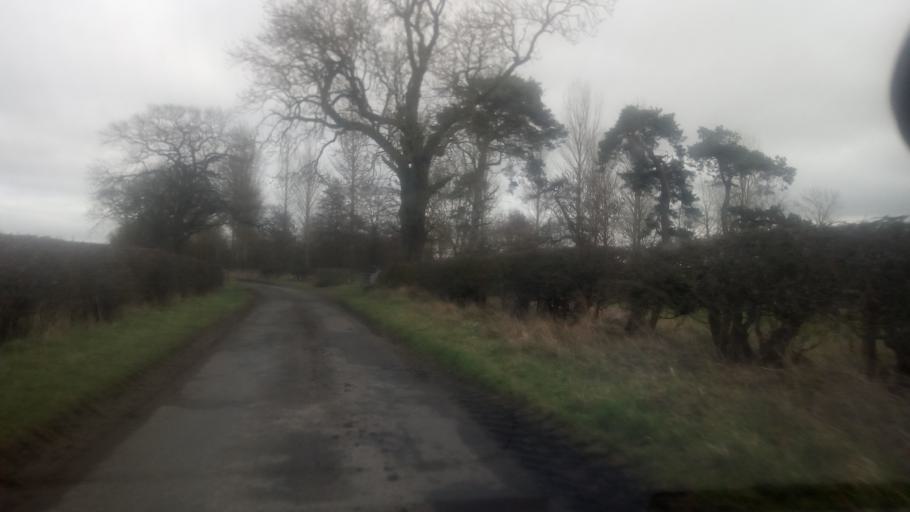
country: GB
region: Scotland
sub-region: The Scottish Borders
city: Kelso
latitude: 55.5665
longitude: -2.4948
